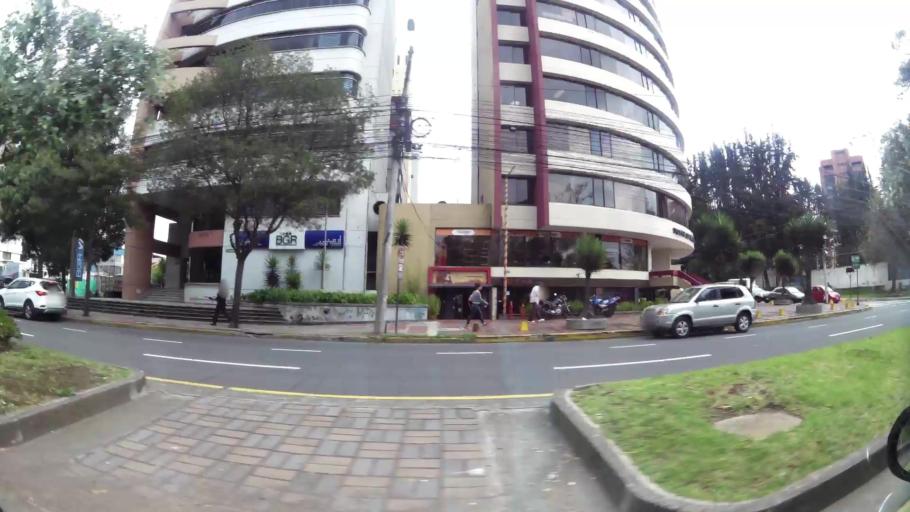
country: EC
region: Pichincha
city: Quito
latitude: -0.1836
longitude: -78.4869
